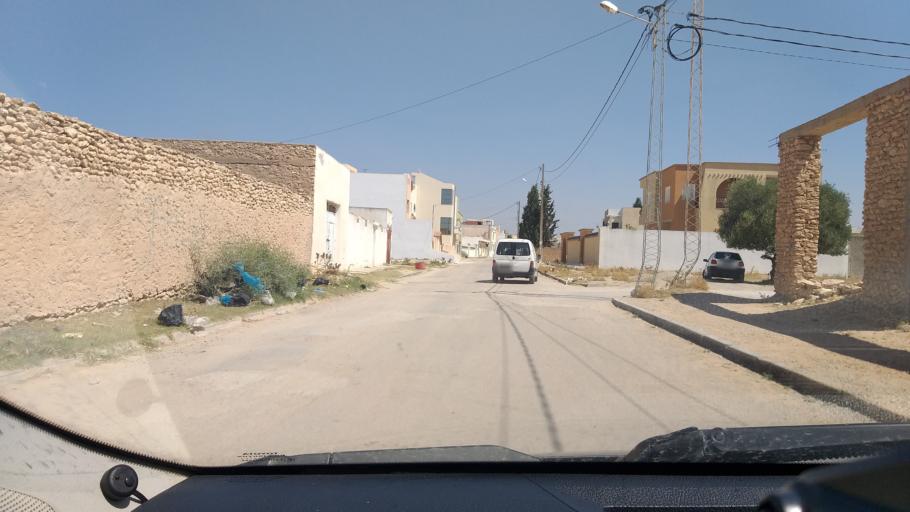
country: TN
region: Al Mahdiyah
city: El Jem
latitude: 35.2908
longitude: 10.7161
